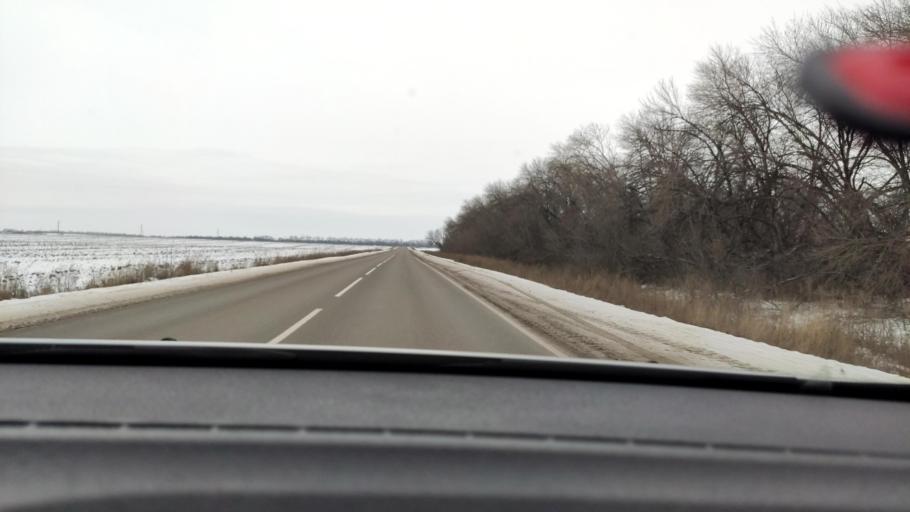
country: RU
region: Voronezj
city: Semiluki
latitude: 51.7328
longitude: 38.9605
